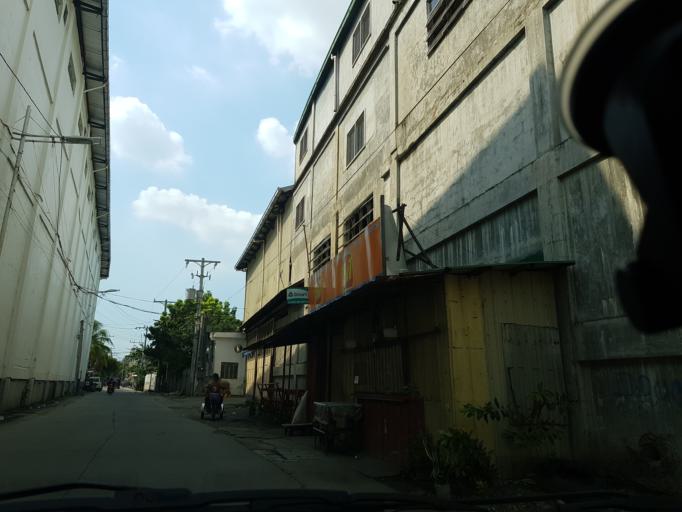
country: PH
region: Calabarzon
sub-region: Province of Rizal
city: Pateros
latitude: 14.5445
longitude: 121.0849
